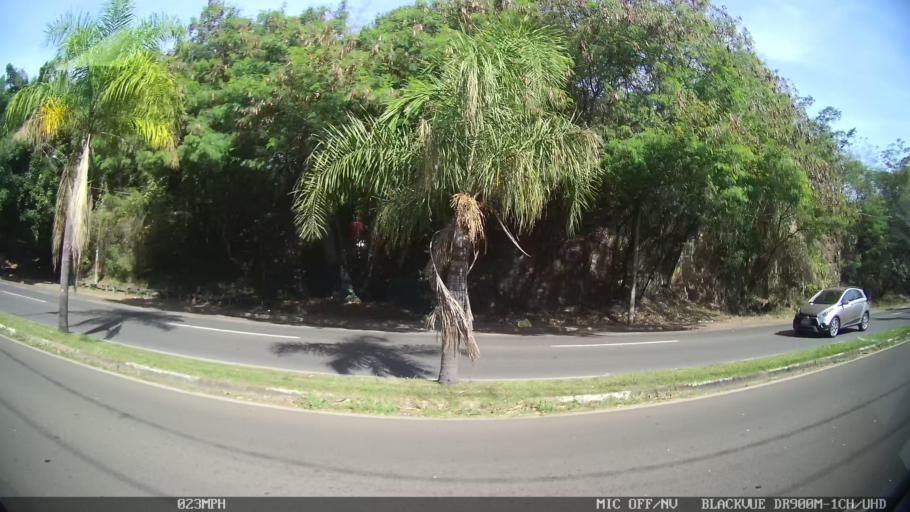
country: BR
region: Sao Paulo
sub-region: Piracicaba
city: Piracicaba
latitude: -22.7272
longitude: -47.6677
